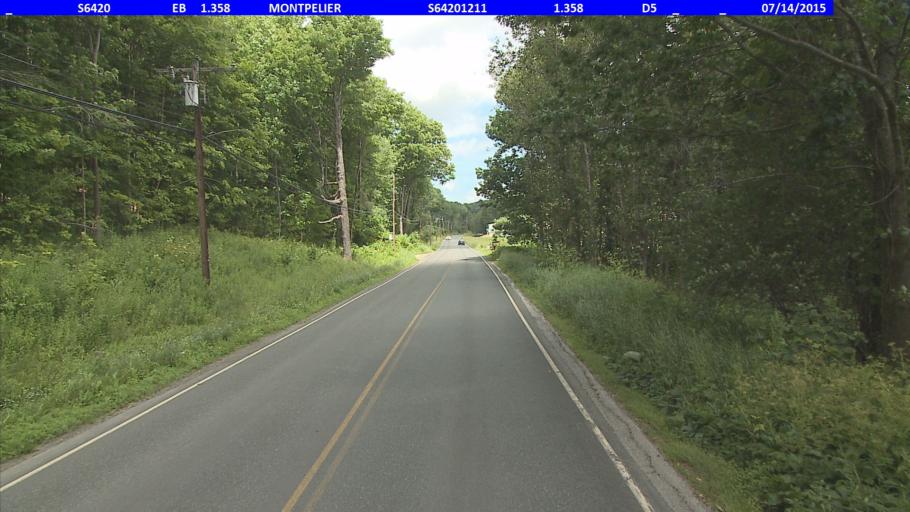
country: US
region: Vermont
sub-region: Washington County
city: Montpelier
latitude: 44.2688
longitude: -72.5579
